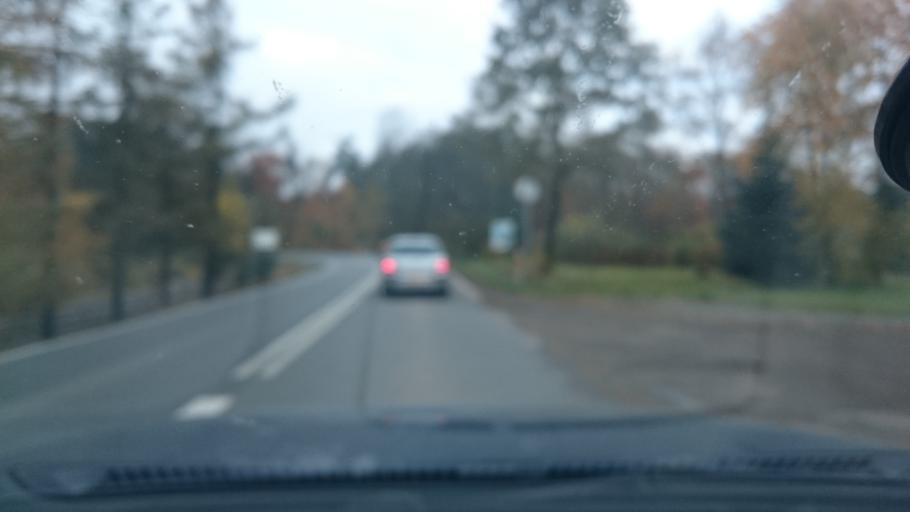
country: PL
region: Silesian Voivodeship
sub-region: Rybnik
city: Rybnik
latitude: 50.1068
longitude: 18.5710
